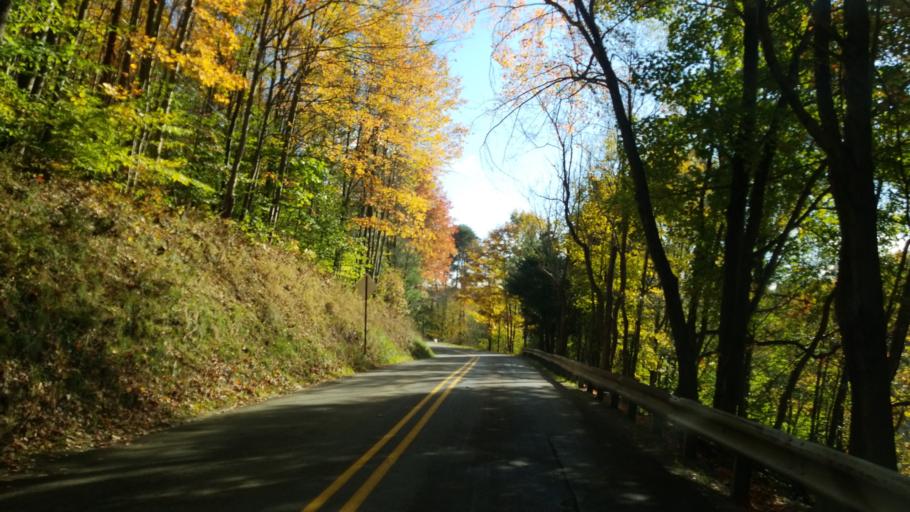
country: US
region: Pennsylvania
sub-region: Jefferson County
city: Albion
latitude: 40.9757
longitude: -78.8687
